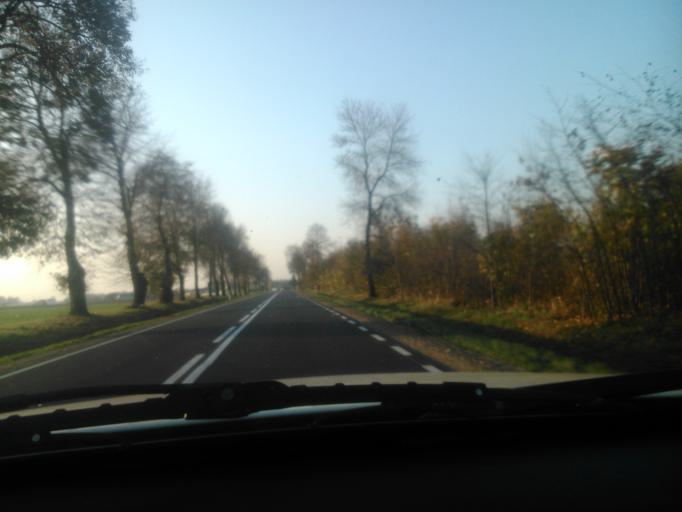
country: PL
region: Masovian Voivodeship
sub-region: Powiat ciechanowski
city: Grudusk
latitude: 53.0703
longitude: 20.5646
